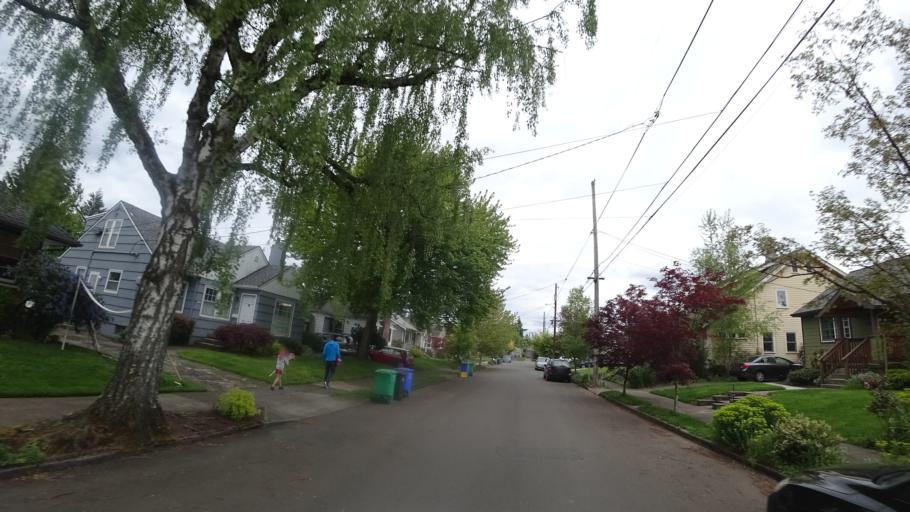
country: US
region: Oregon
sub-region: Clackamas County
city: Milwaukie
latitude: 45.4694
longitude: -122.6442
